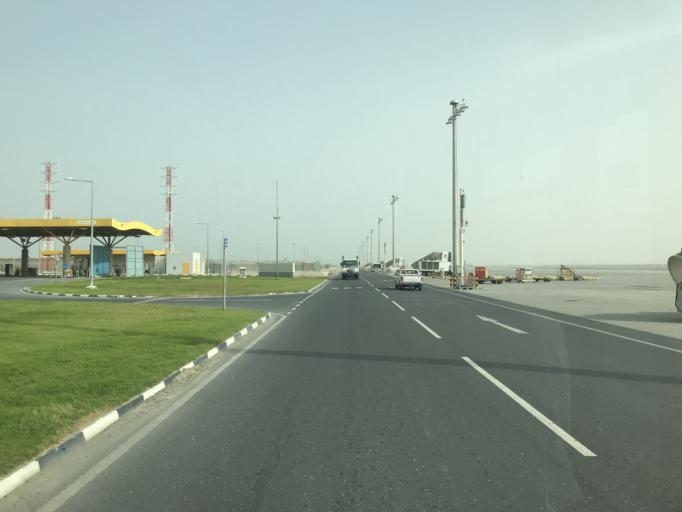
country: QA
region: Baladiyat ad Dawhah
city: Doha
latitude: 25.2775
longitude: 51.5996
